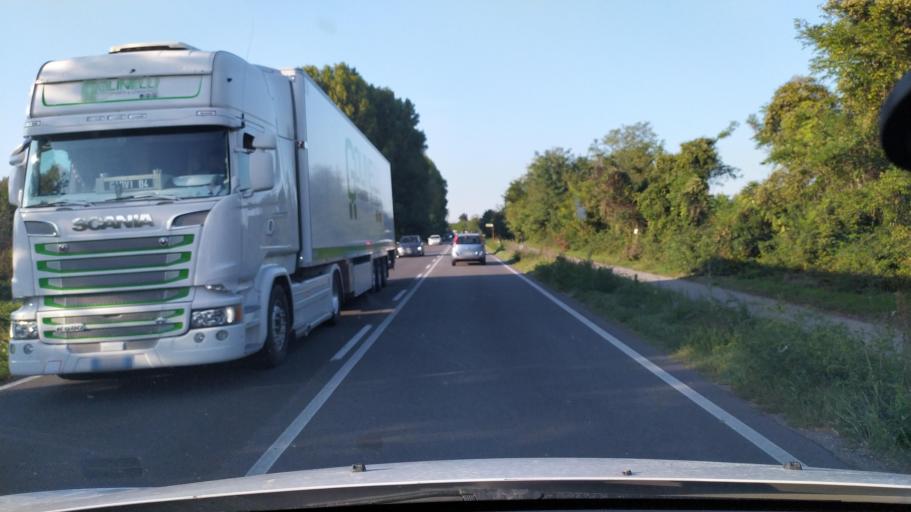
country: IT
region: Lombardy
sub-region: Citta metropolitana di Milano
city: Cisliano
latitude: 45.4597
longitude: 8.9694
